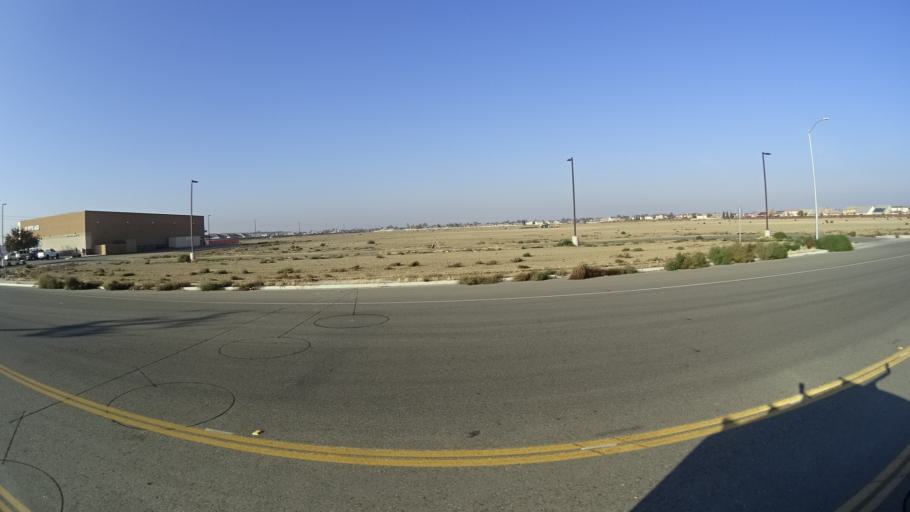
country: US
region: California
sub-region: Kern County
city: Greenacres
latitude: 35.2975
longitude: -119.1097
